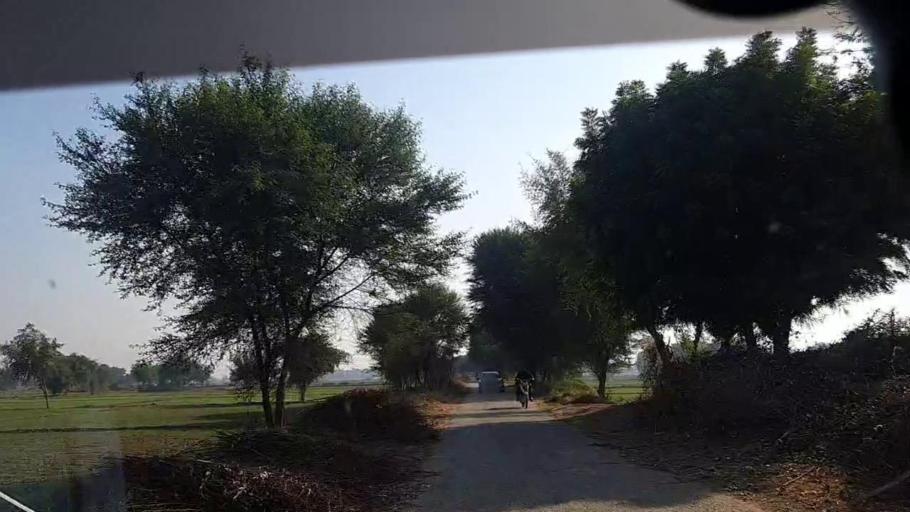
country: PK
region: Sindh
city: Hingorja
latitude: 27.2276
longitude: 68.2689
